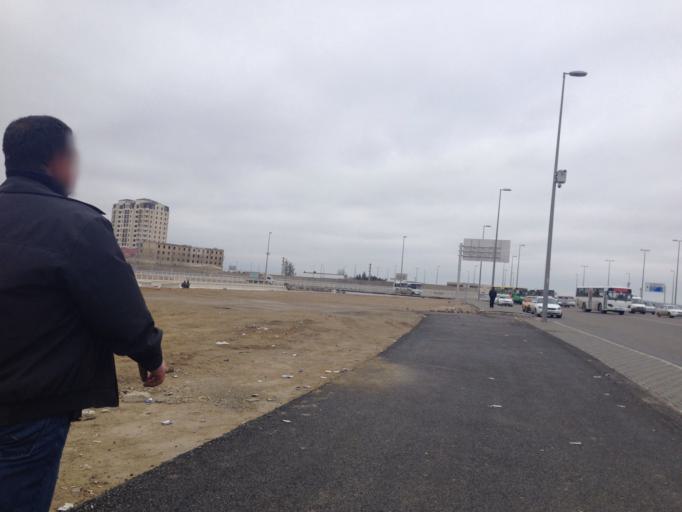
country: AZ
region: Baki
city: Sabuncu
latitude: 40.4234
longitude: 49.9174
